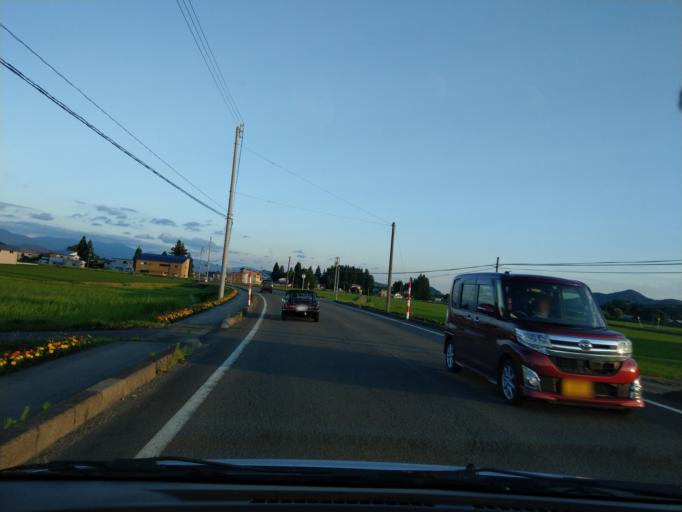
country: JP
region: Akita
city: Kakunodatemachi
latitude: 39.6450
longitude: 140.5704
